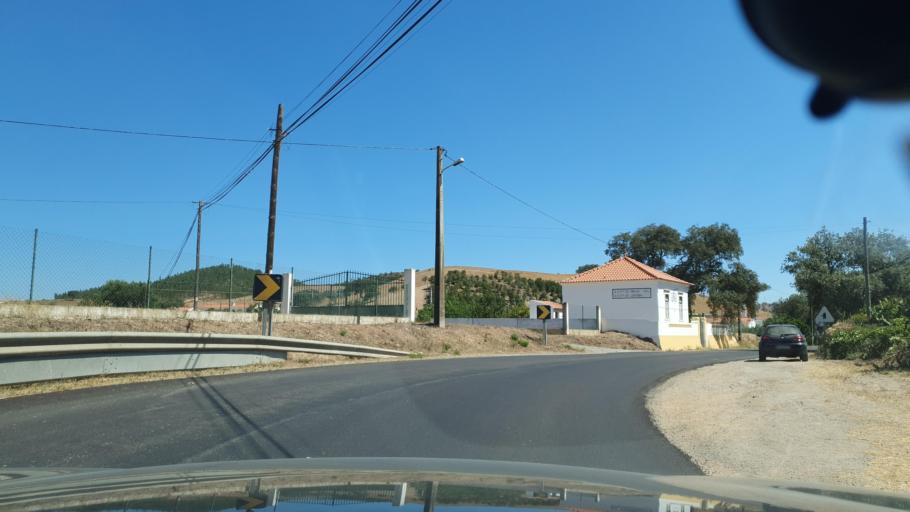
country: PT
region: Faro
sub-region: Monchique
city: Monchique
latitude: 37.4839
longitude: -8.4884
